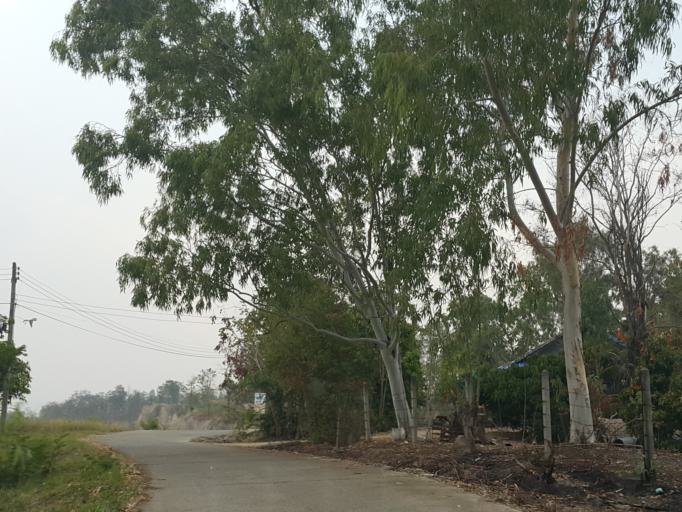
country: TH
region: Chiang Mai
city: Mae Taeng
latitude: 18.9684
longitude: 98.9354
